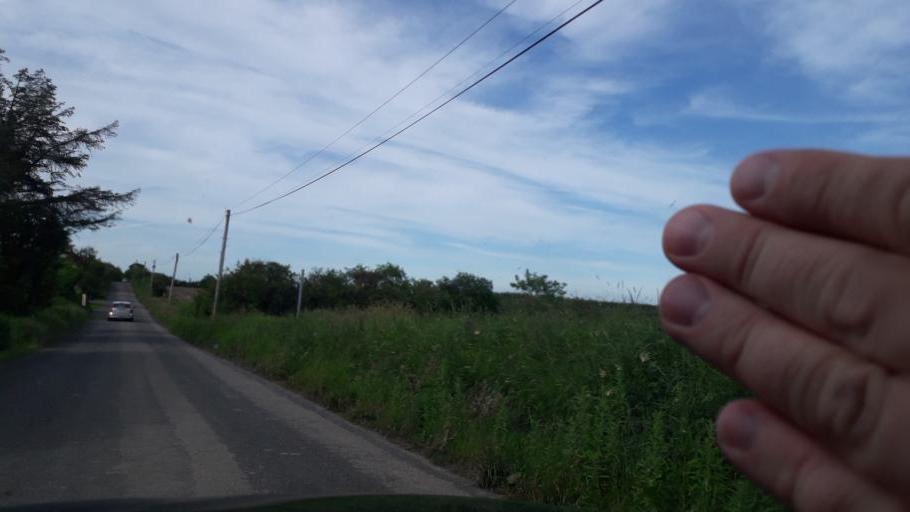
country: IE
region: Leinster
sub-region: Loch Garman
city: Courtown
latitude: 52.5234
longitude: -6.2717
